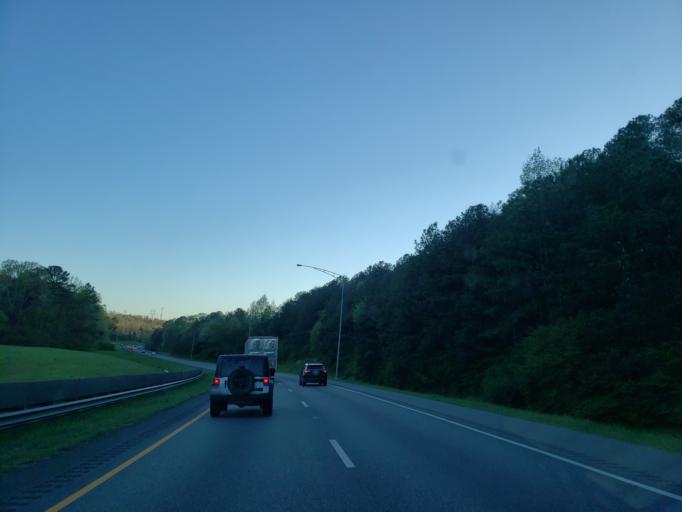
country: US
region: Alabama
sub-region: Jefferson County
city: Bessemer
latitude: 33.3407
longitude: -87.0324
